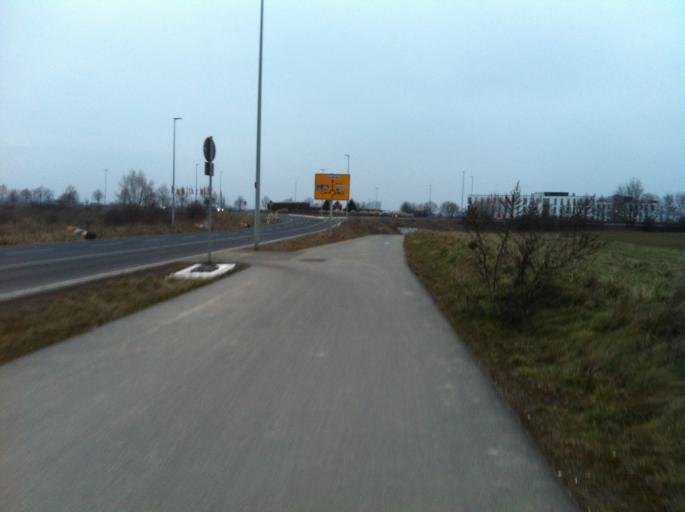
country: DE
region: Rheinland-Pfalz
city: Klein-Winternheim
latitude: 49.9898
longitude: 8.2202
